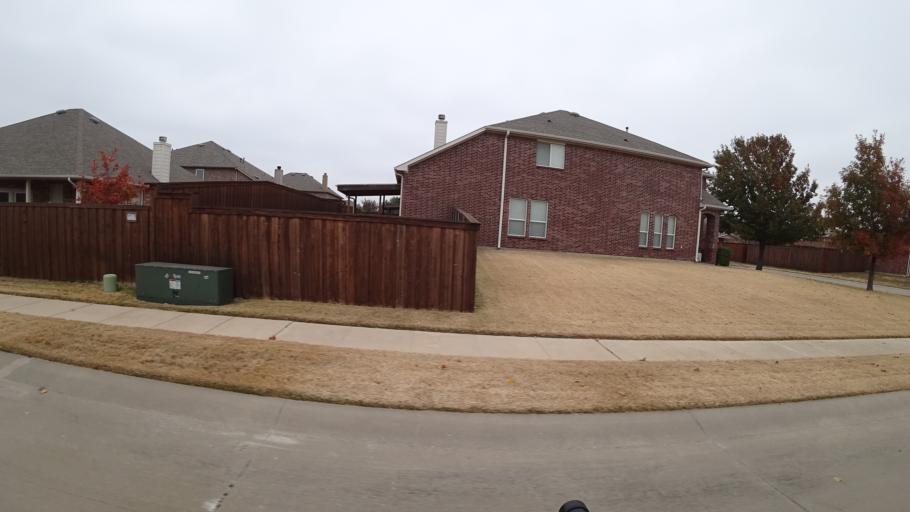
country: US
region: Texas
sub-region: Denton County
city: The Colony
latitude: 33.0682
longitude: -96.9068
